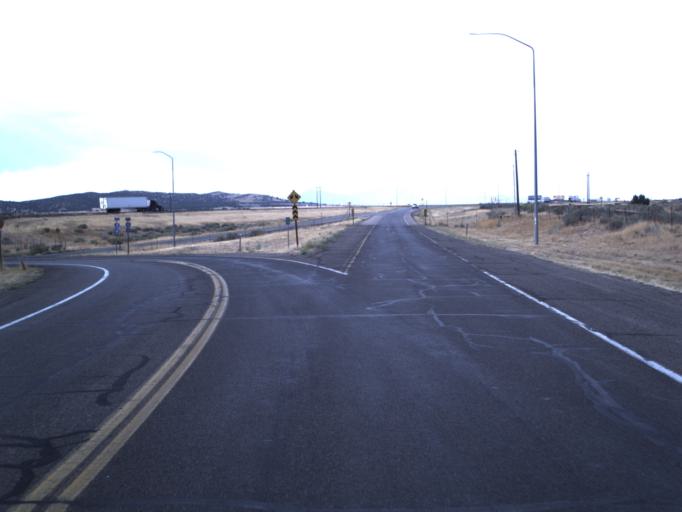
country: US
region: Utah
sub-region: Millard County
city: Fillmore
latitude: 38.9903
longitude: -112.3228
